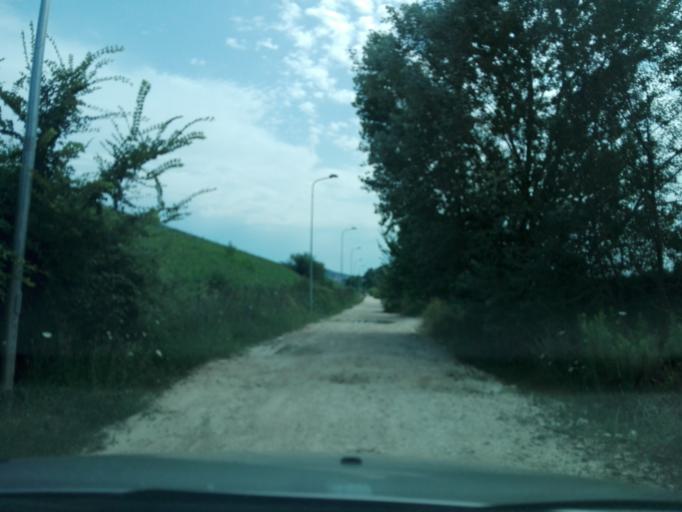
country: IT
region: Abruzzo
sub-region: Provincia di Pescara
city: Cappelle sul Tavo
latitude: 42.4916
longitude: 14.1125
